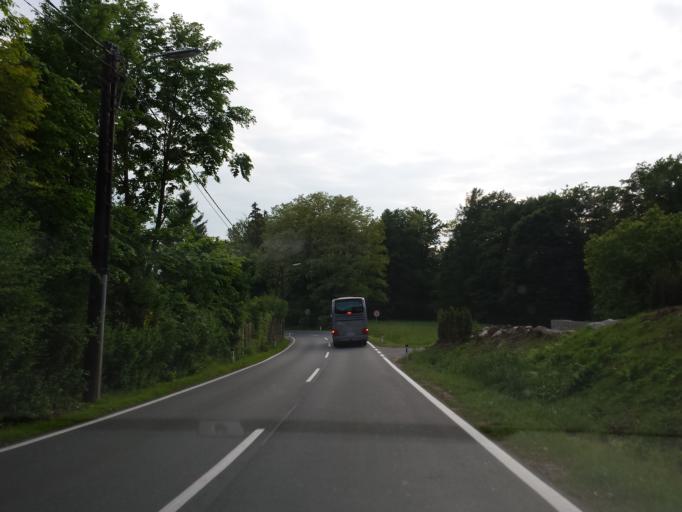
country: AT
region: Styria
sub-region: Graz Stadt
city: Mariatrost
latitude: 47.0907
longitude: 15.5038
